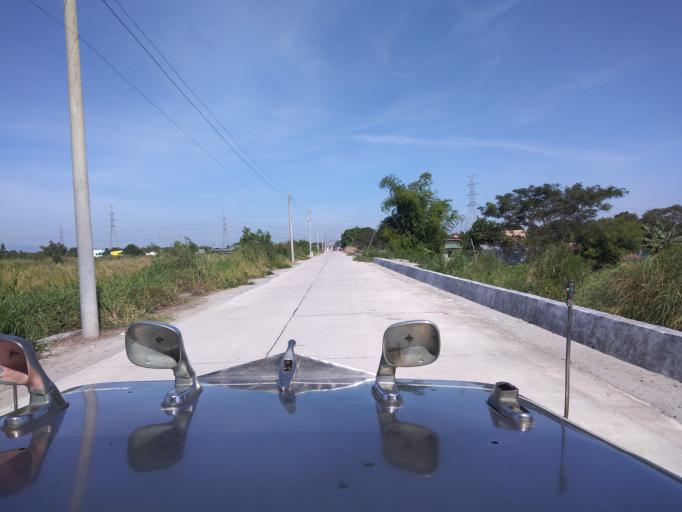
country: PH
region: Central Luzon
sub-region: Province of Pampanga
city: Bacolor
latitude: 15.0038
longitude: 120.6602
